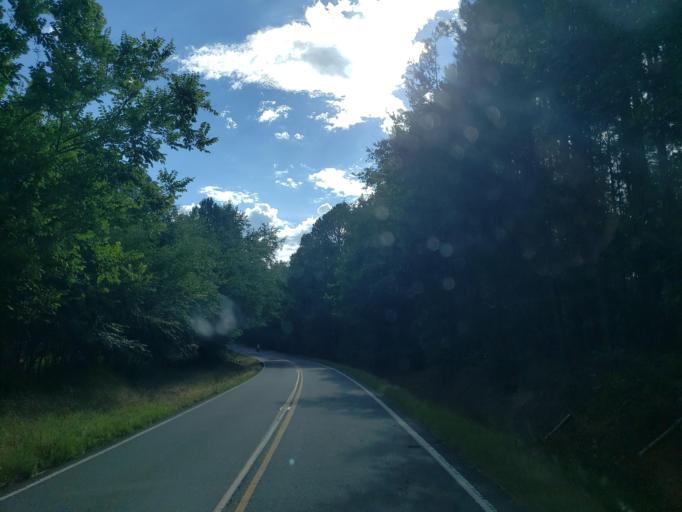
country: US
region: Georgia
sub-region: Floyd County
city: Lindale
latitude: 34.2023
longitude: -85.0981
